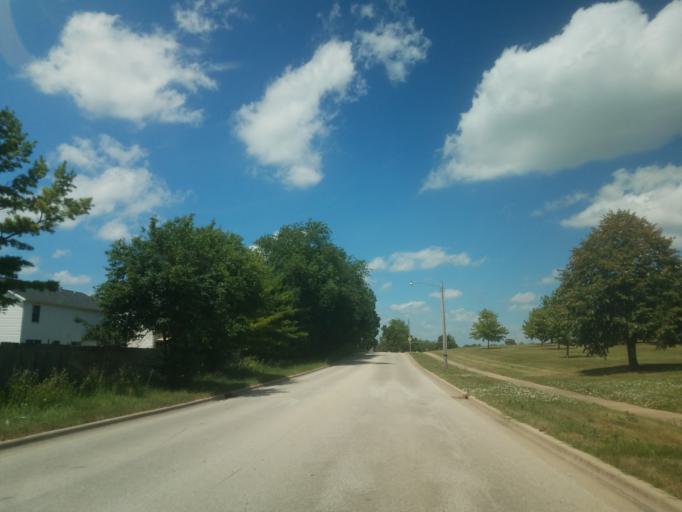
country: US
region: Illinois
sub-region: McLean County
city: Bloomington
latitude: 40.4494
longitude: -89.0296
